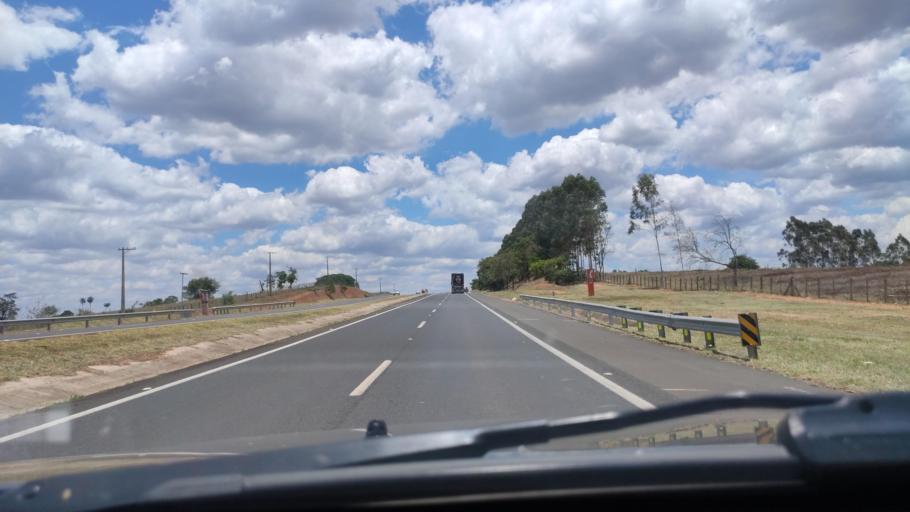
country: BR
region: Sao Paulo
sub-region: Duartina
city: Duartina
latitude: -22.4996
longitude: -49.2727
